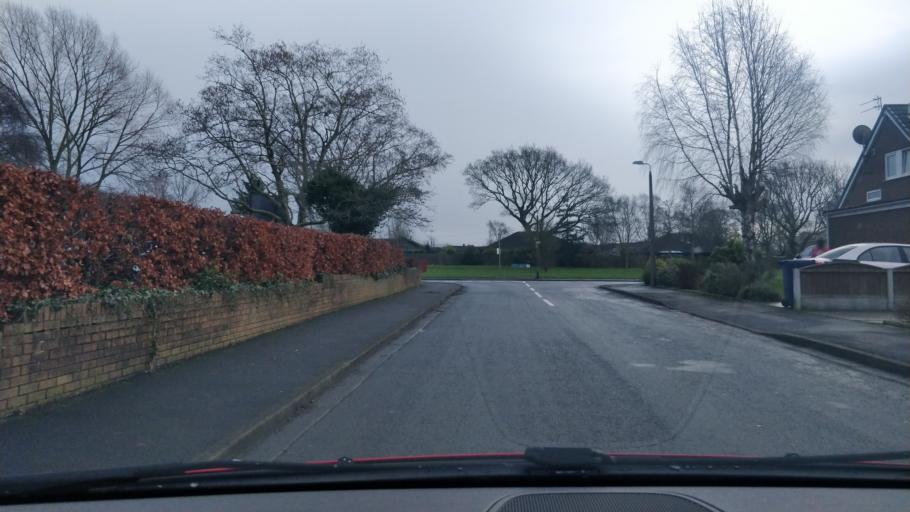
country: GB
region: England
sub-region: Lancashire
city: Preston
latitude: 53.7406
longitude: -2.7407
